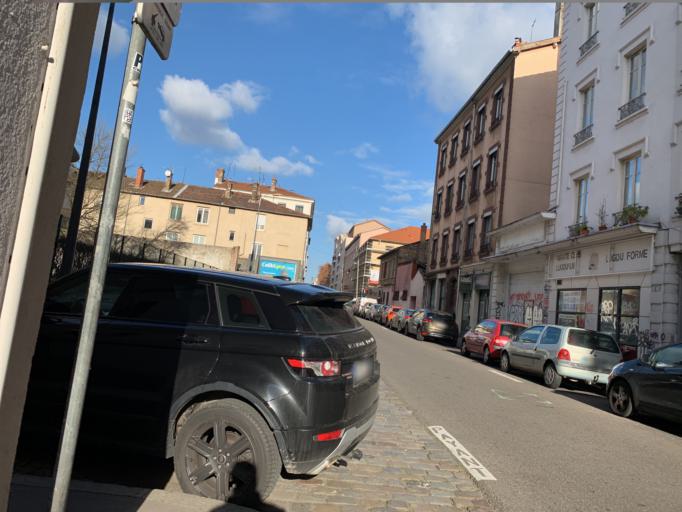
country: FR
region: Rhone-Alpes
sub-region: Departement du Rhone
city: Villeurbanne
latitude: 45.7560
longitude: 4.8671
